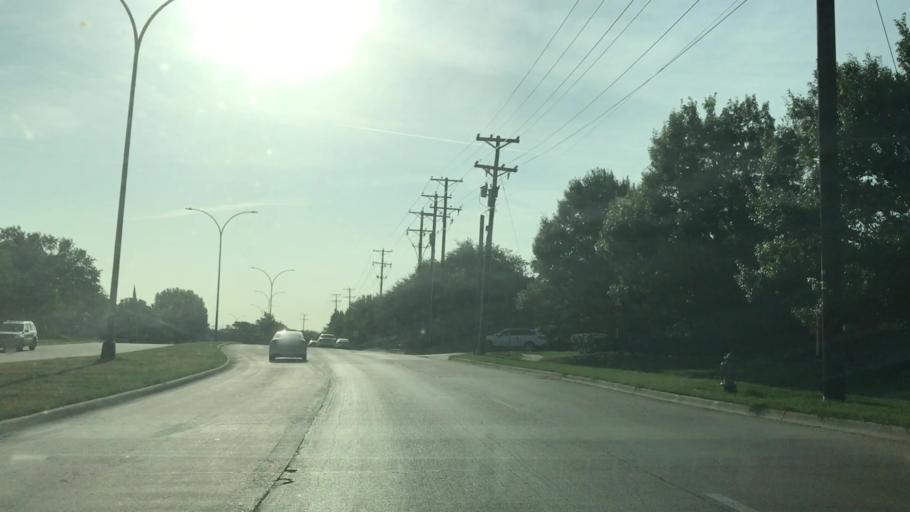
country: US
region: Texas
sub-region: Tarrant County
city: Arlington
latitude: 32.7760
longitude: -97.0806
